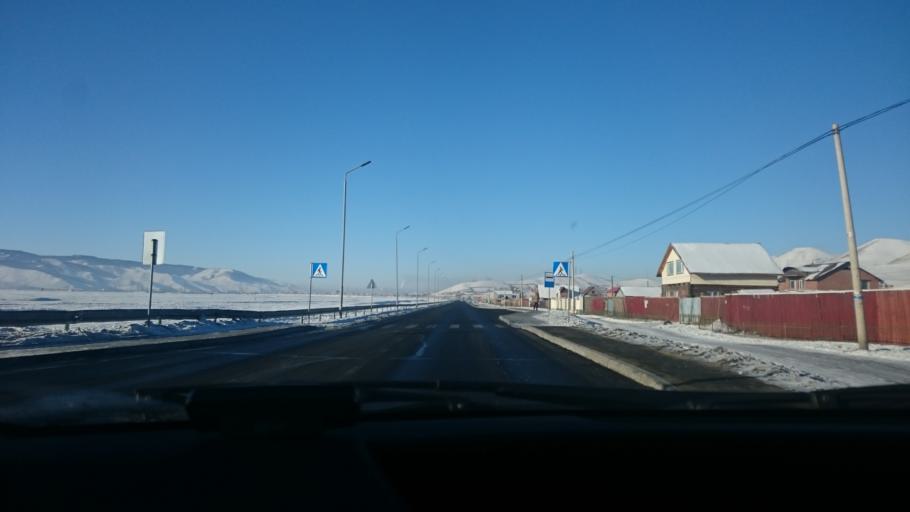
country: MN
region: Ulaanbaatar
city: Ulaanbaatar
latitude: 47.9157
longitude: 107.0768
